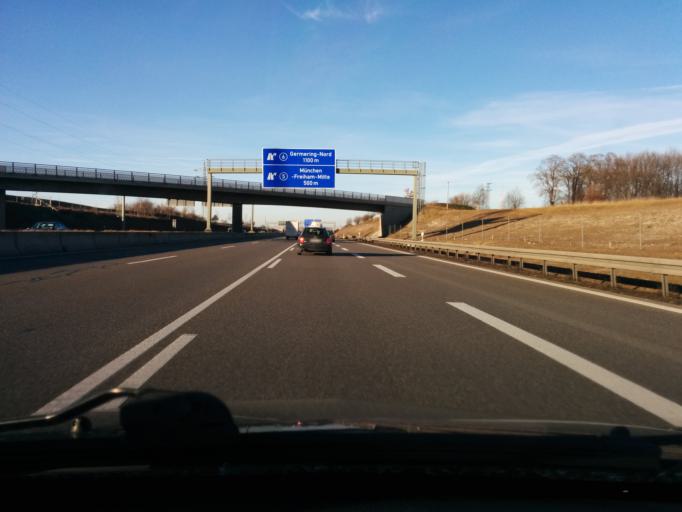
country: DE
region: Bavaria
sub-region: Upper Bavaria
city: Germering
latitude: 48.1324
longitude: 11.4005
